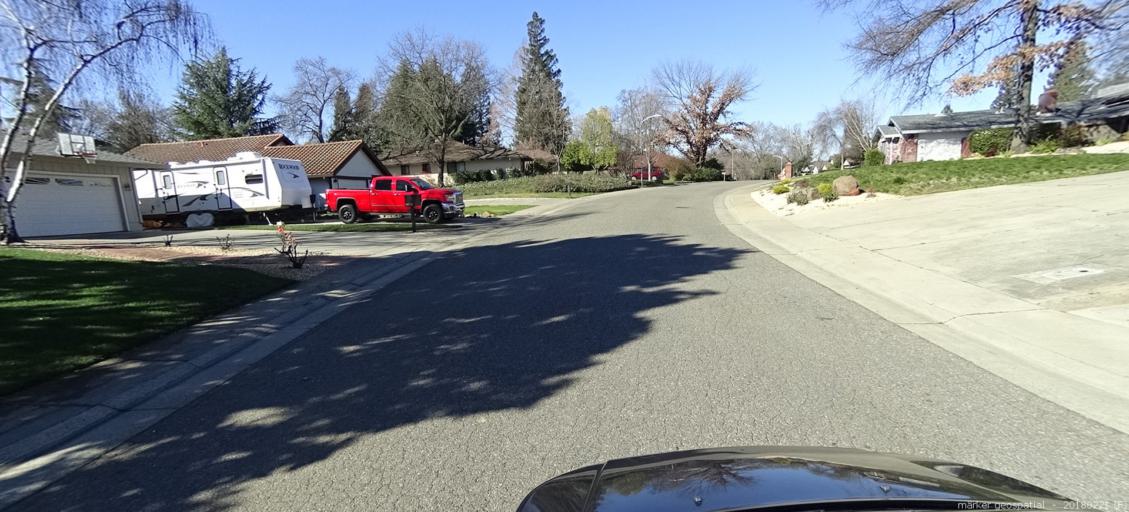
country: US
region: California
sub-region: Sacramento County
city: Orangevale
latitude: 38.6819
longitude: -121.2383
